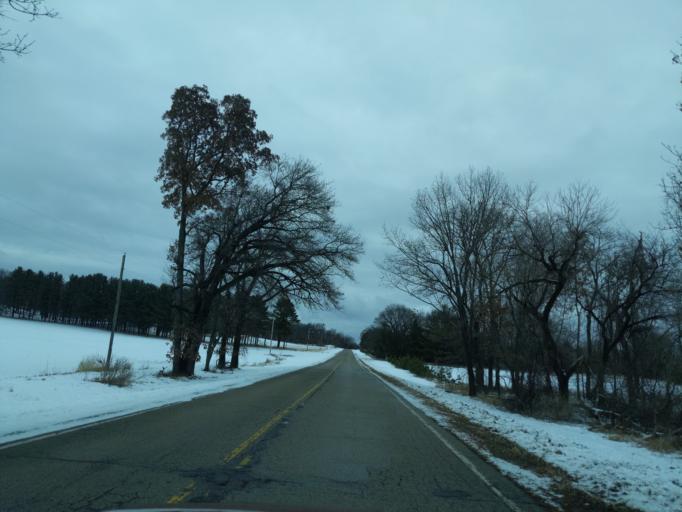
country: US
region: Wisconsin
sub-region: Marquette County
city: Montello
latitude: 43.9134
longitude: -89.3529
